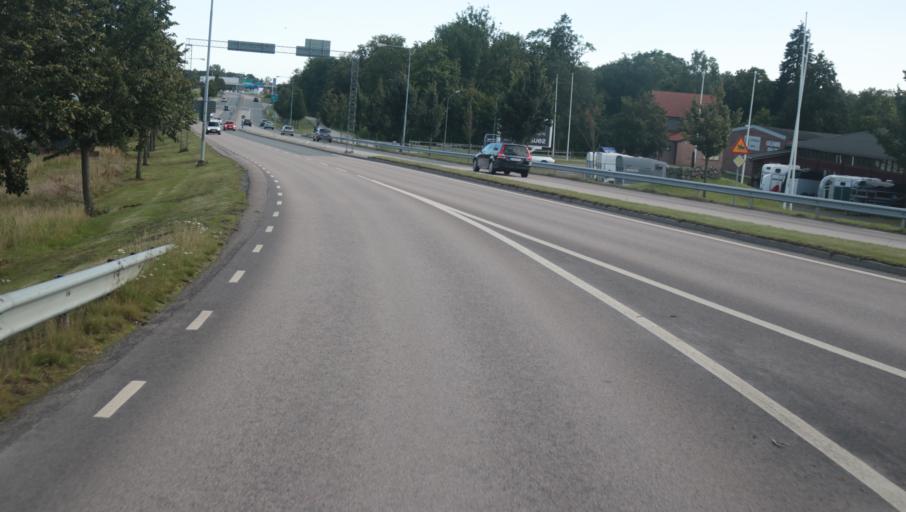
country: SE
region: Blekinge
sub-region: Karlshamns Kommun
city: Karlshamn
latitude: 56.1937
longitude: 14.8425
